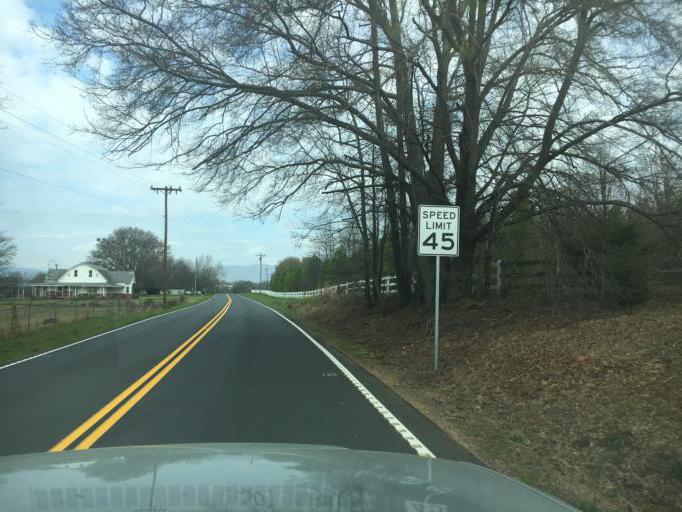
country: US
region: South Carolina
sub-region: Spartanburg County
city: Landrum
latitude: 35.0866
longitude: -82.1933
